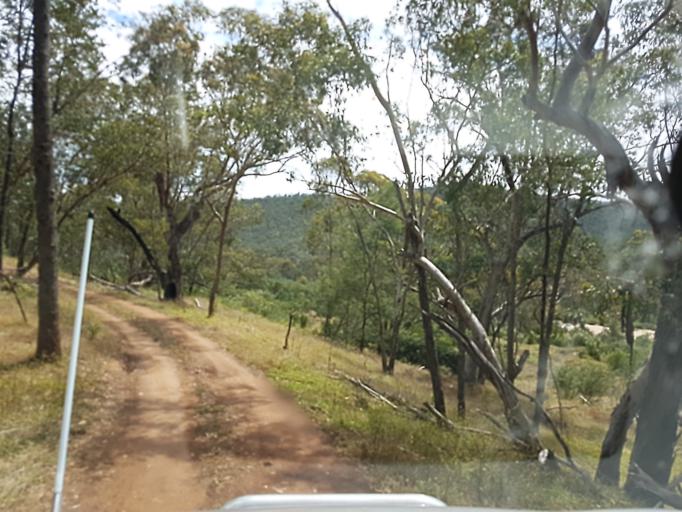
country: AU
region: New South Wales
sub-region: Snowy River
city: Jindabyne
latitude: -36.9373
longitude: 148.4000
